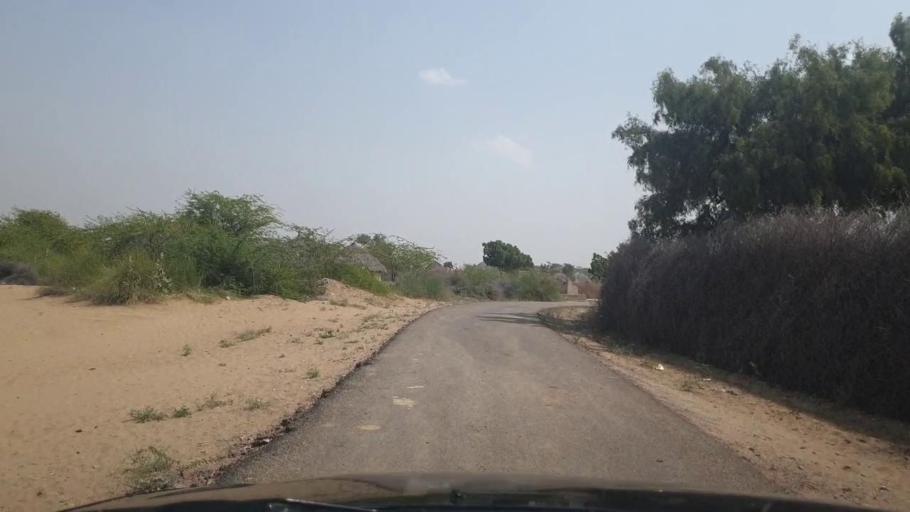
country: PK
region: Sindh
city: Islamkot
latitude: 25.0051
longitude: 70.4141
